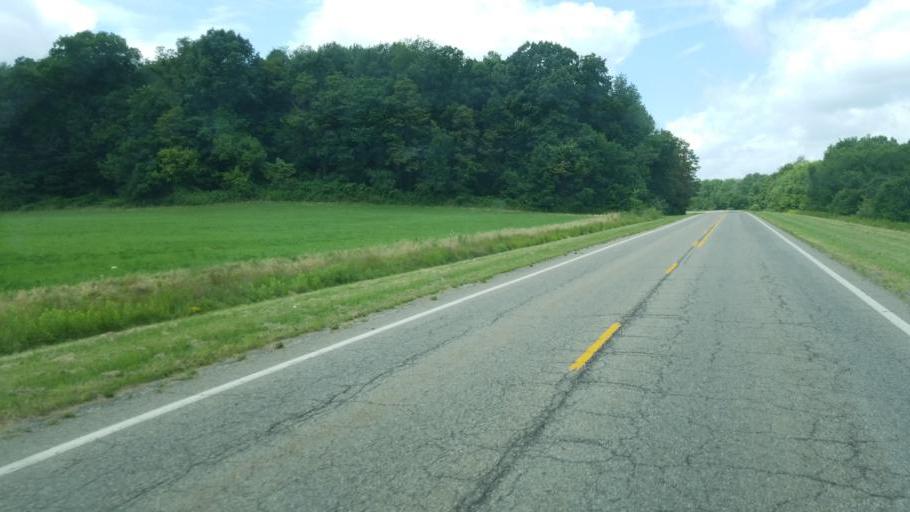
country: US
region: Ohio
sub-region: Columbiana County
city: New Waterford
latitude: 40.7954
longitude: -80.6469
